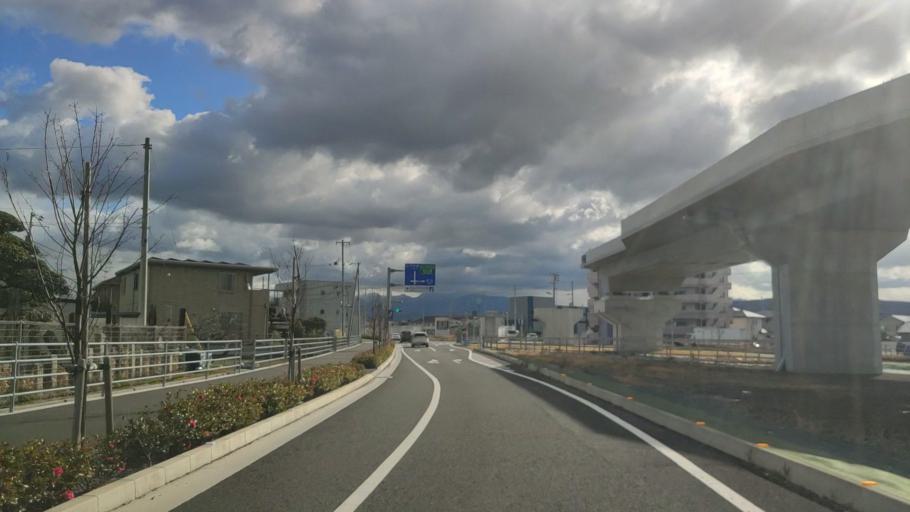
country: JP
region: Ehime
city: Masaki-cho
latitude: 33.8123
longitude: 132.7232
